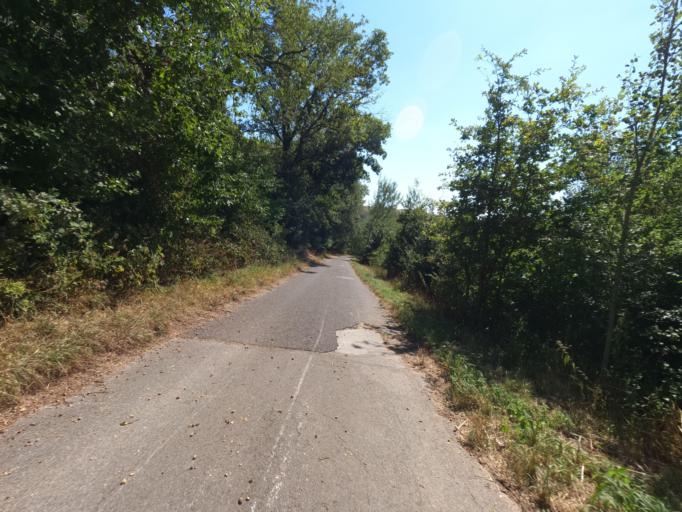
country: DE
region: North Rhine-Westphalia
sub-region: Regierungsbezirk Koln
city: Wassenberg
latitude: 51.0880
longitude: 6.1939
